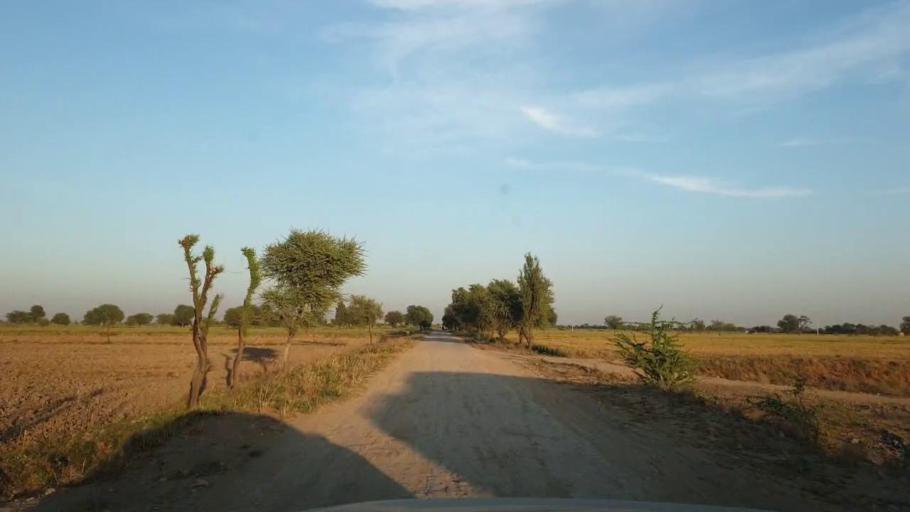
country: PK
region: Sindh
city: Kunri
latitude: 25.1289
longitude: 69.4381
